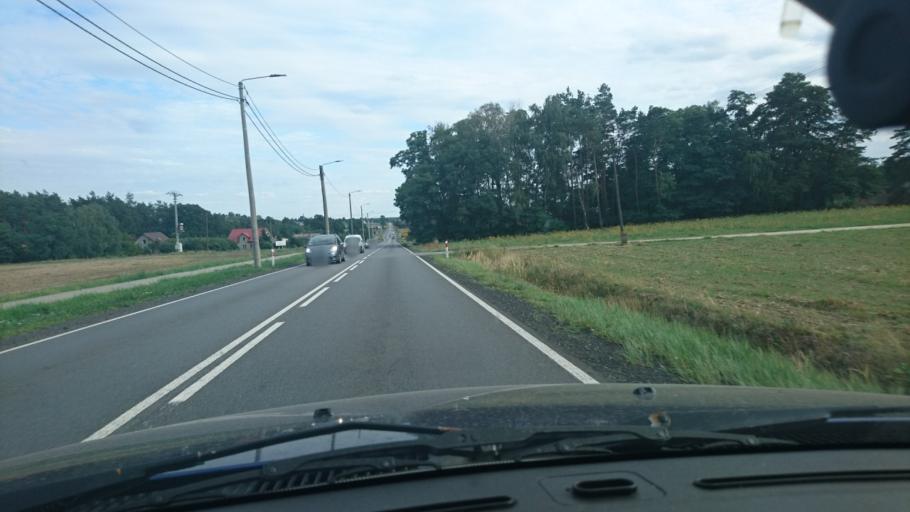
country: PL
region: Greater Poland Voivodeship
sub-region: Powiat ostrzeszowski
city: Ostrzeszow
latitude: 51.4017
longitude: 17.9377
